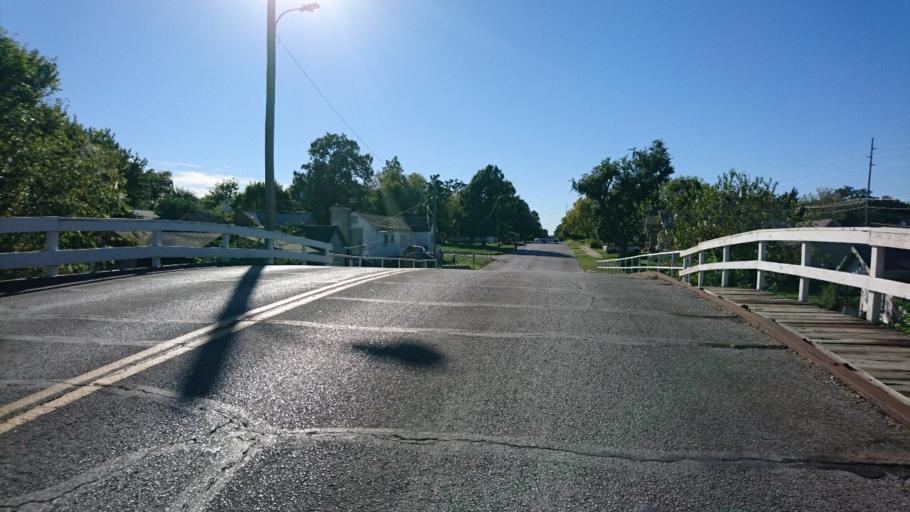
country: US
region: Missouri
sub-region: Jasper County
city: Carthage
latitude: 37.1765
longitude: -94.3183
